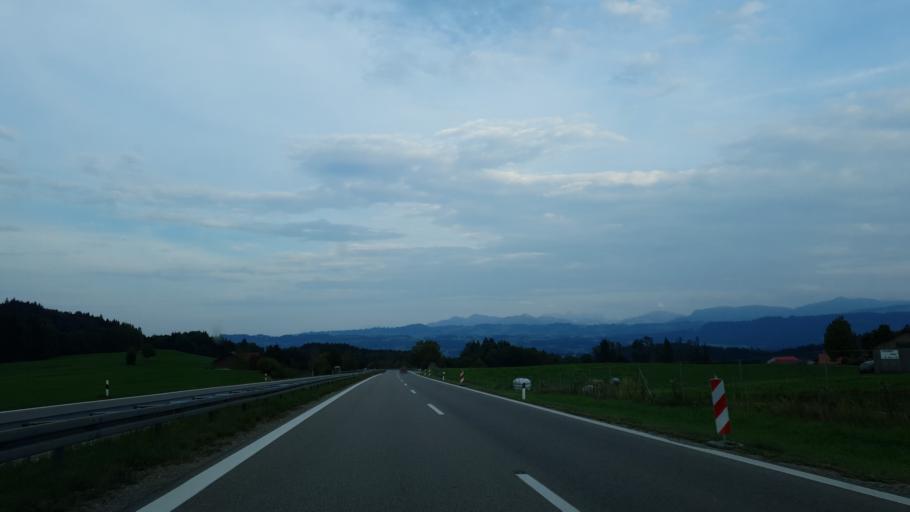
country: DE
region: Bavaria
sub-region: Swabia
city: Buchenberg
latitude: 47.6700
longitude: 10.2430
